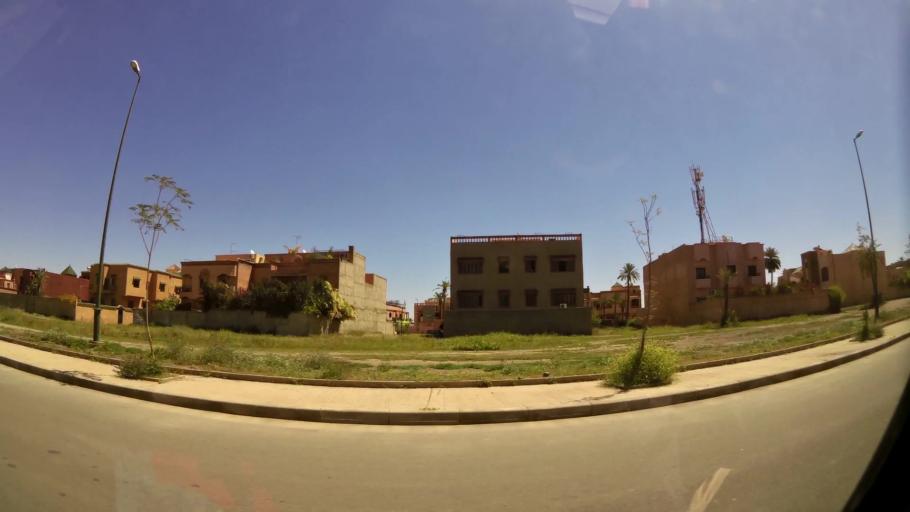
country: MA
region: Marrakech-Tensift-Al Haouz
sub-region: Marrakech
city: Marrakesh
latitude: 31.6490
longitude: -7.9893
